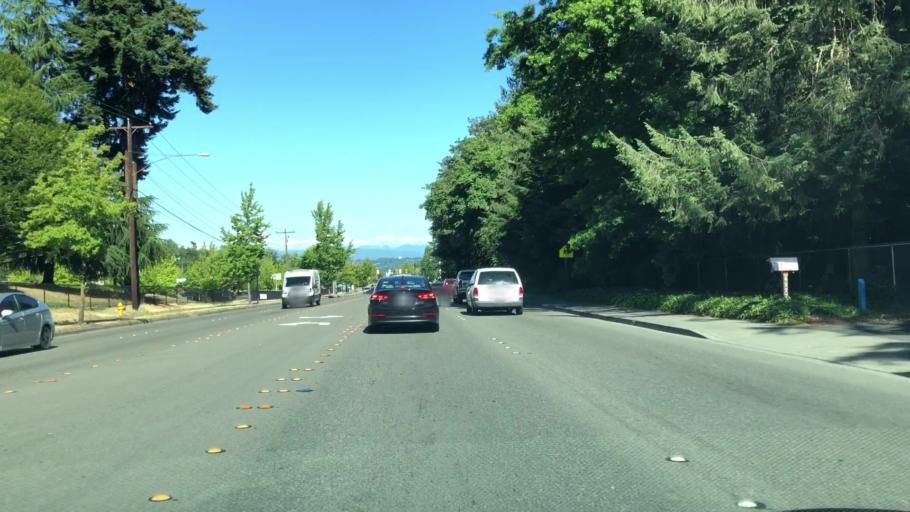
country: US
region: Washington
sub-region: King County
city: SeaTac
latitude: 47.4343
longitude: -122.2800
